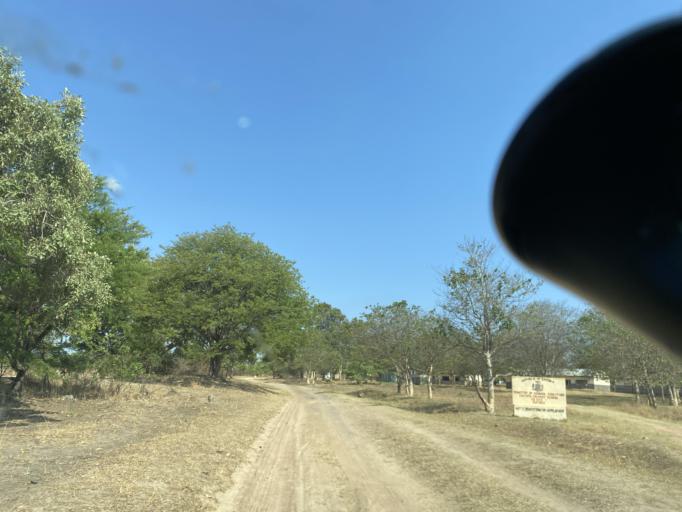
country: ZM
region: Lusaka
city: Chongwe
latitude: -15.2157
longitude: 28.8362
